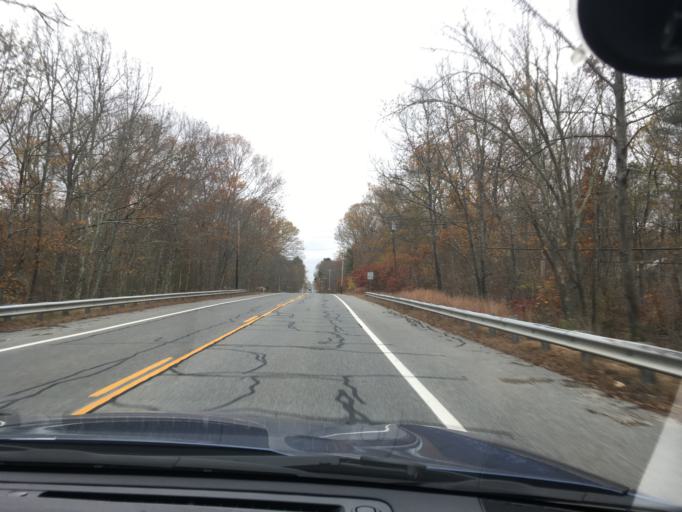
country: US
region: Rhode Island
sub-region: Providence County
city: Foster
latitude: 41.8461
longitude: -71.7019
